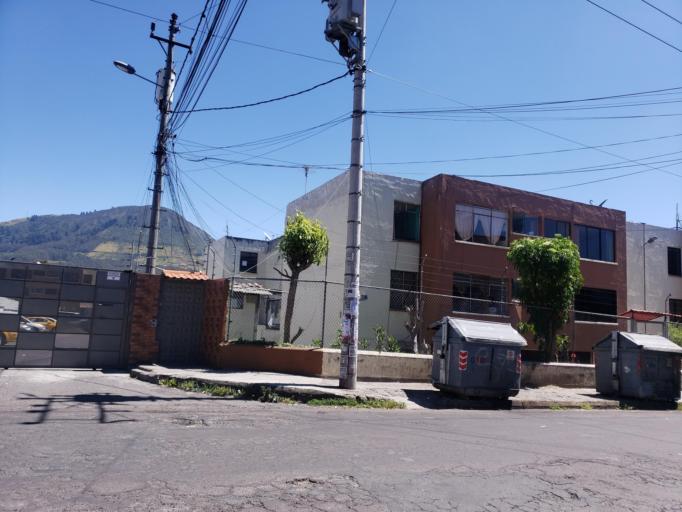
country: EC
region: Pichincha
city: Quito
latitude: -0.2643
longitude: -78.5380
